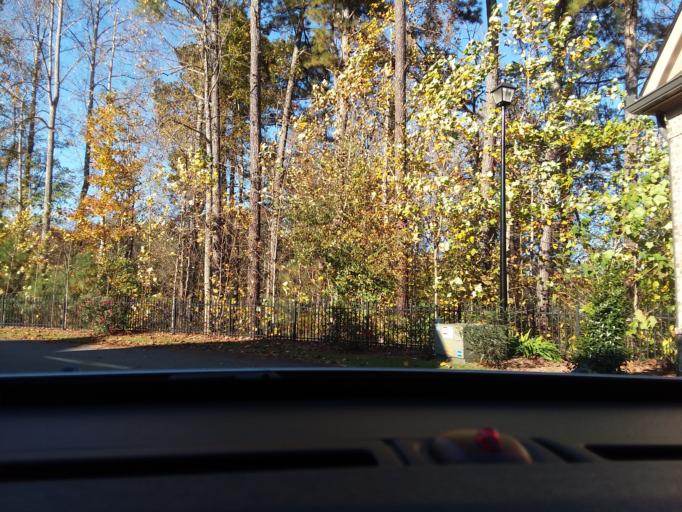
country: US
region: Georgia
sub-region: Fulton County
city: Johns Creek
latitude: 34.0020
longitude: -84.2671
